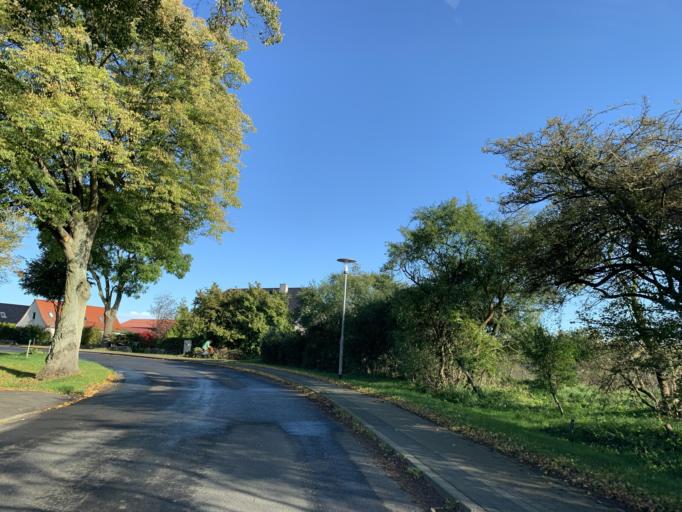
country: DE
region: Mecklenburg-Vorpommern
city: Burg Stargard
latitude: 53.4879
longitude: 13.2711
